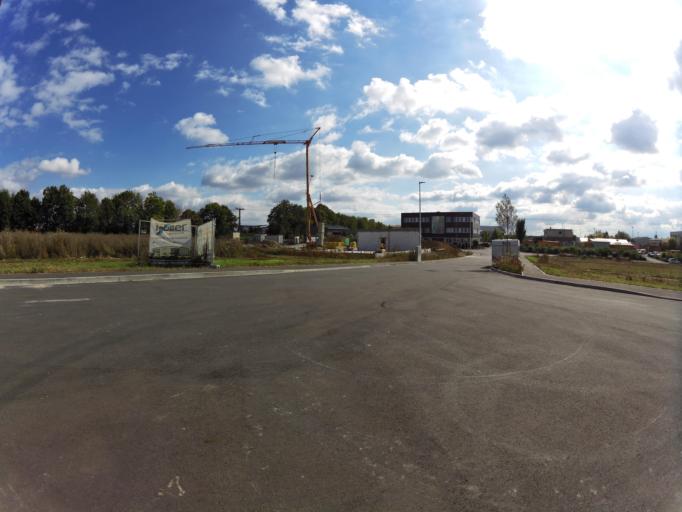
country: DE
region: Bavaria
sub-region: Regierungsbezirk Unterfranken
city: Waldbuttelbrunn
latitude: 49.7976
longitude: 9.8418
